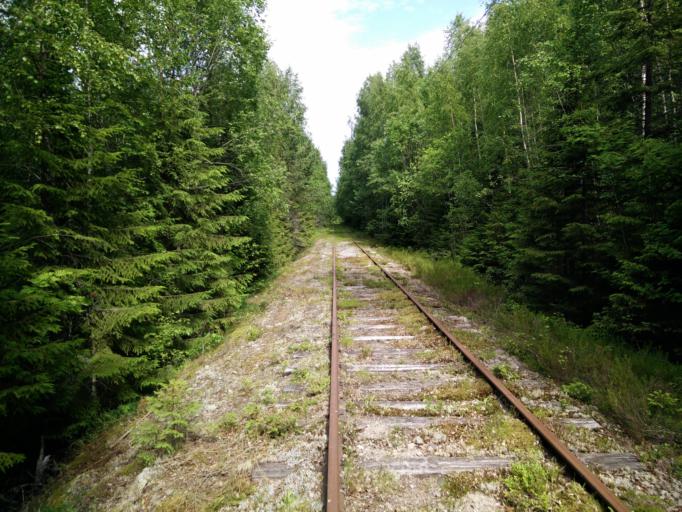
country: SE
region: Gaevleborg
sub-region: Hudiksvalls Kommun
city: Delsbo
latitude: 61.7999
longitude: 16.3979
